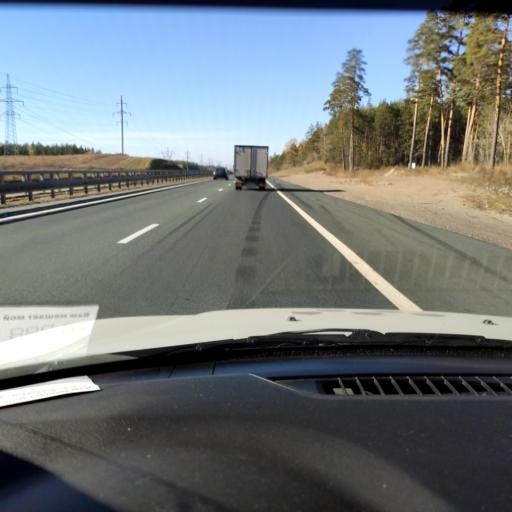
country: RU
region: Samara
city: Povolzhskiy
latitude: 53.5172
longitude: 49.7515
